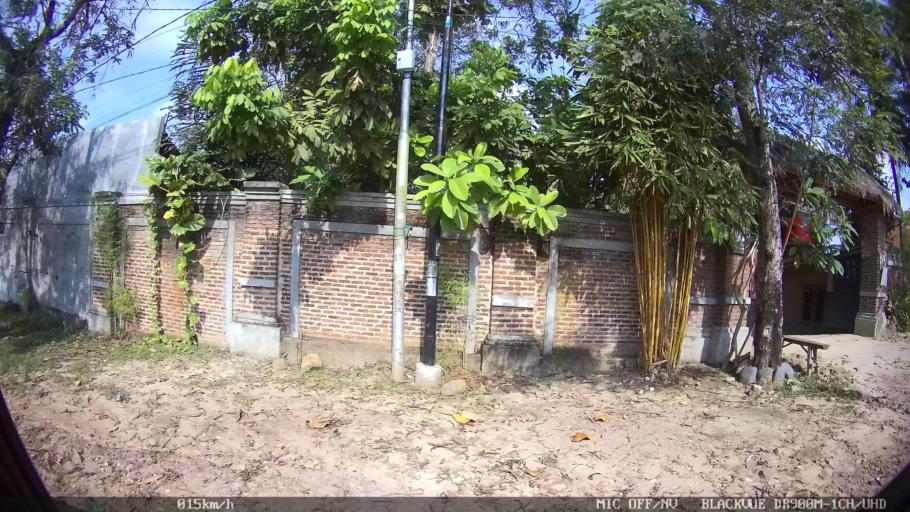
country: ID
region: Lampung
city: Kedaton
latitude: -5.3847
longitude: 105.2303
